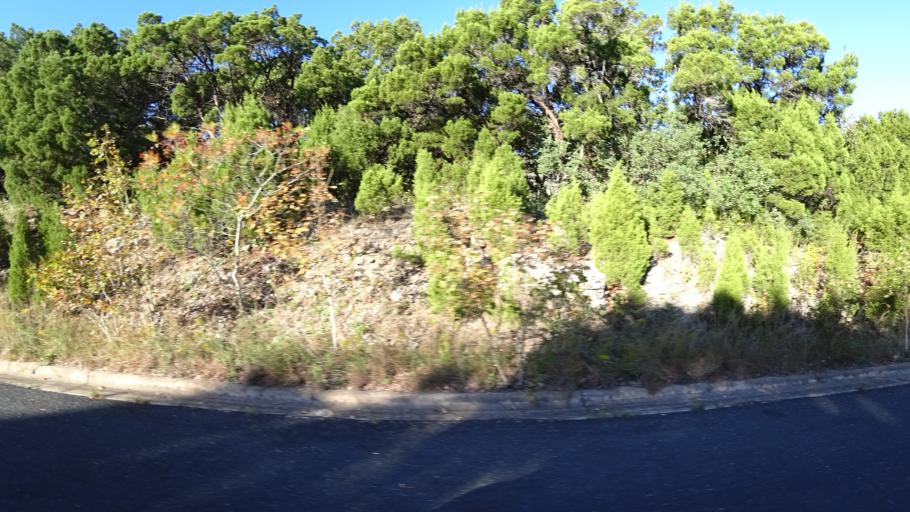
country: US
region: Texas
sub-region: Travis County
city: West Lake Hills
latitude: 30.3602
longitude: -97.8057
